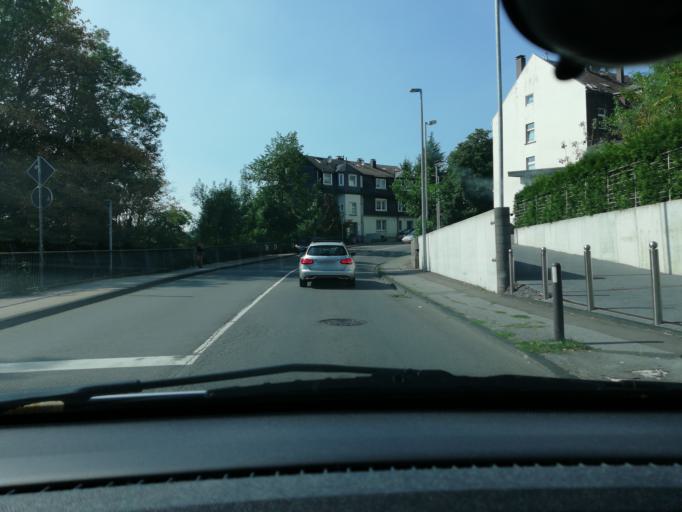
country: DE
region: North Rhine-Westphalia
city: Gevelsberg
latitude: 51.3237
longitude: 7.3377
